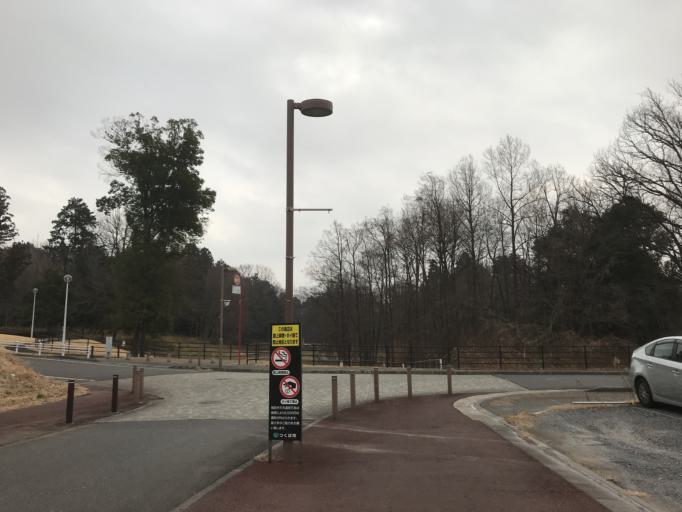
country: JP
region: Ibaraki
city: Mitsukaido
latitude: 36.0289
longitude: 140.0580
